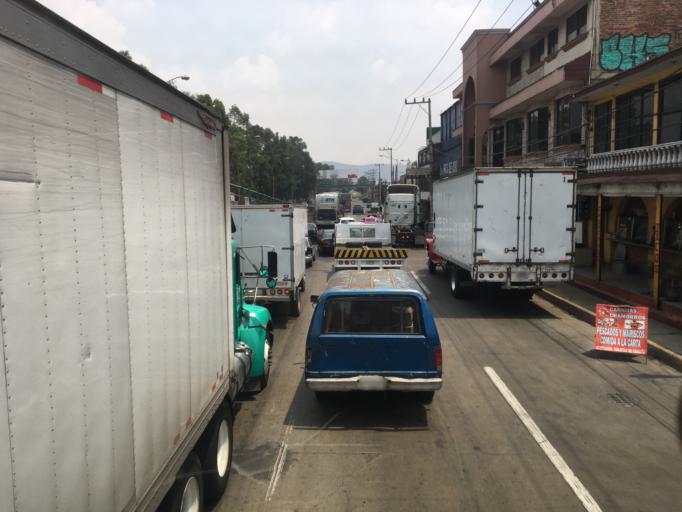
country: MX
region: Mexico
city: Tlalnepantla
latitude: 19.5343
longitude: -99.1806
